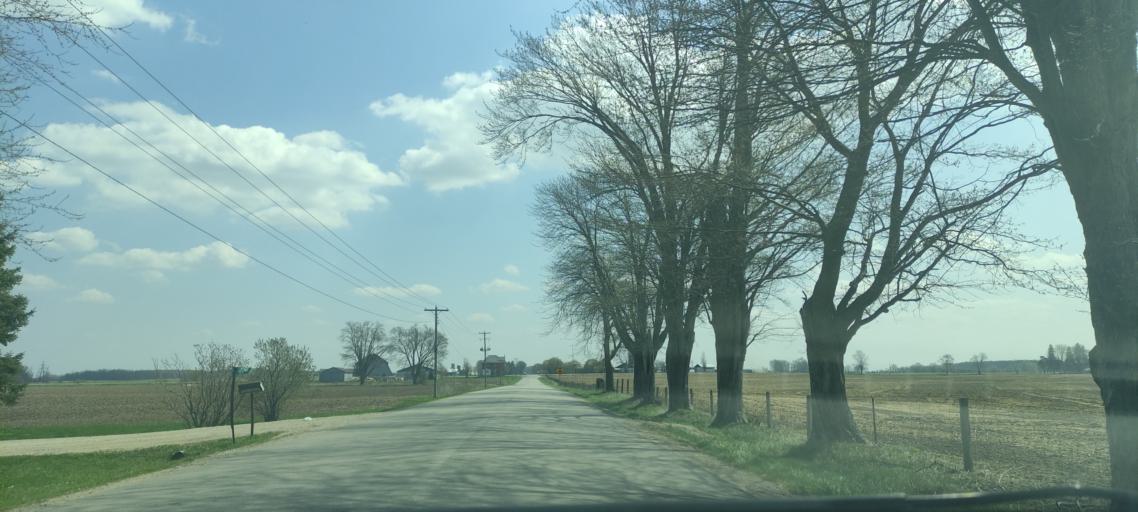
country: CA
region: Ontario
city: Stratford
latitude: 43.3345
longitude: -80.9681
